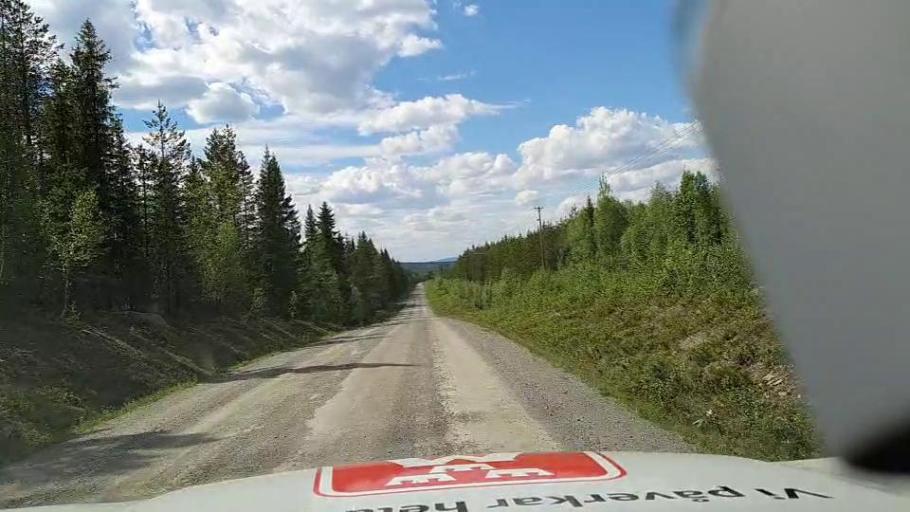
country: SE
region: Vaesterbotten
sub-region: Vilhelmina Kommun
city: Sjoberg
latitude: 64.5419
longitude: 15.6764
